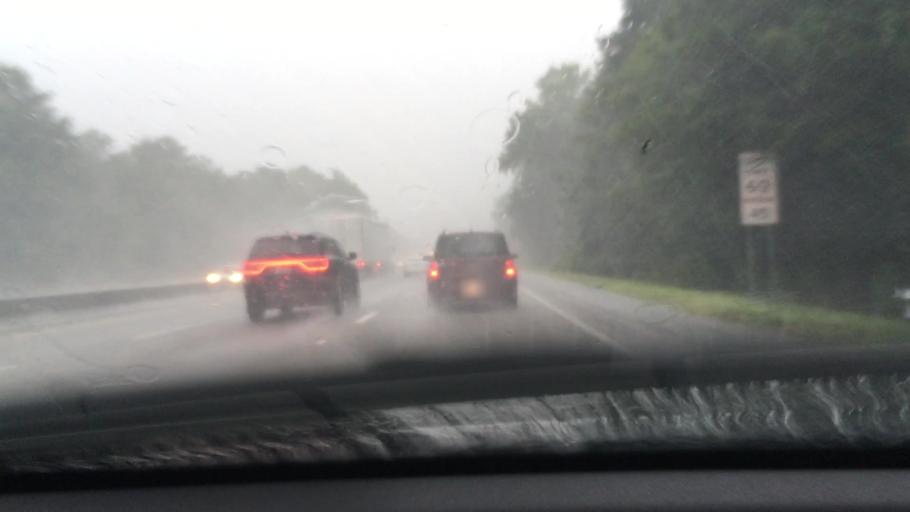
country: US
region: South Carolina
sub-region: Richland County
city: Dentsville
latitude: 34.0713
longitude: -81.0125
